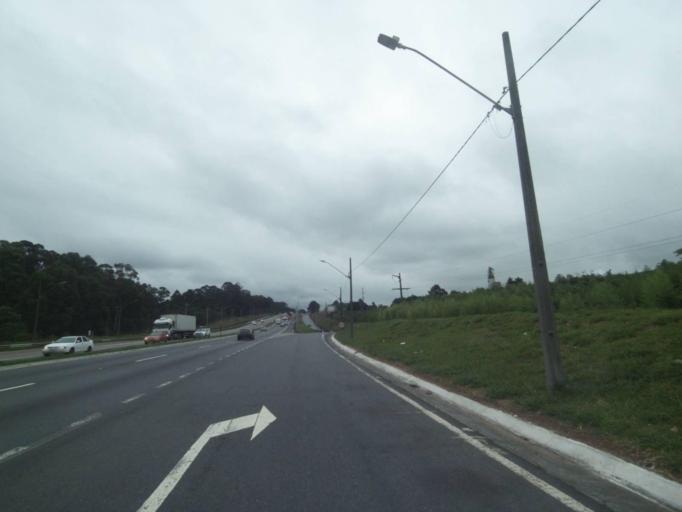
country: BR
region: Parana
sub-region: Araucaria
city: Araucaria
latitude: -25.5564
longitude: -49.3449
